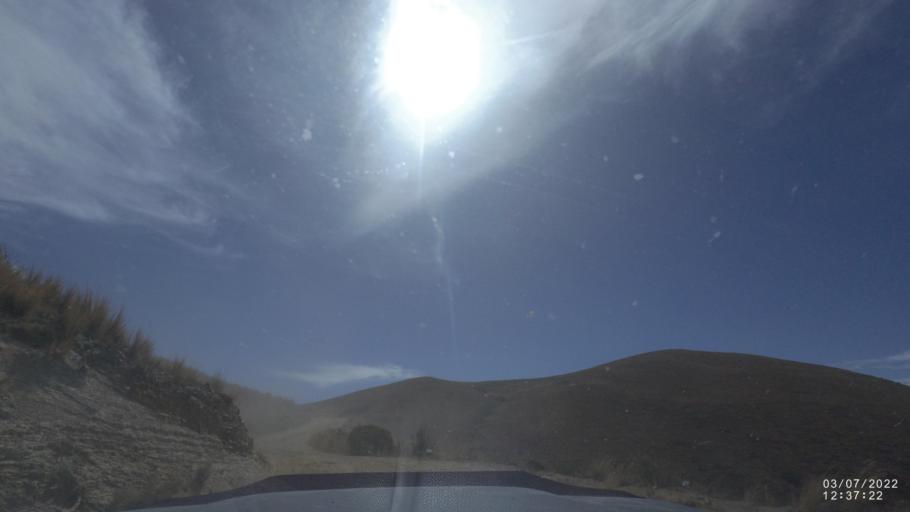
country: BO
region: Cochabamba
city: Irpa Irpa
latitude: -17.7976
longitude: -66.6156
